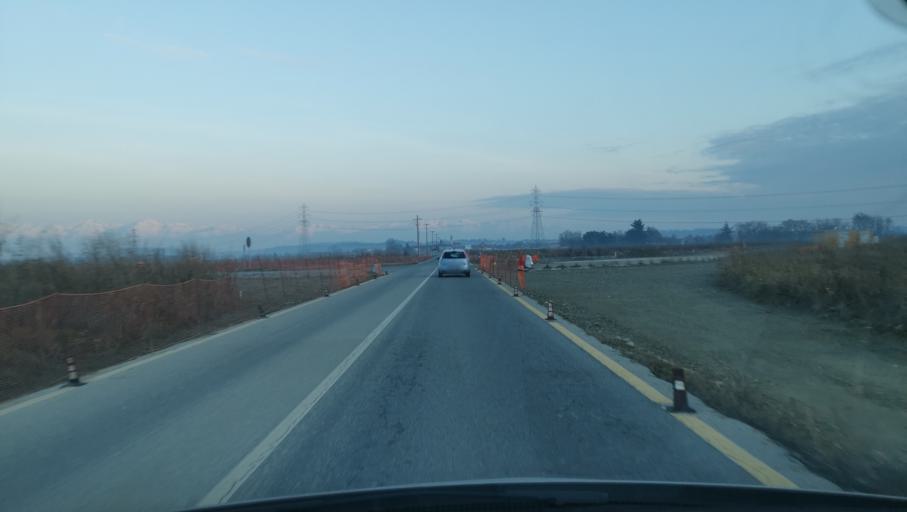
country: IT
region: Piedmont
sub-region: Provincia di Torino
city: Caluso
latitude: 45.2730
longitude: 7.8925
